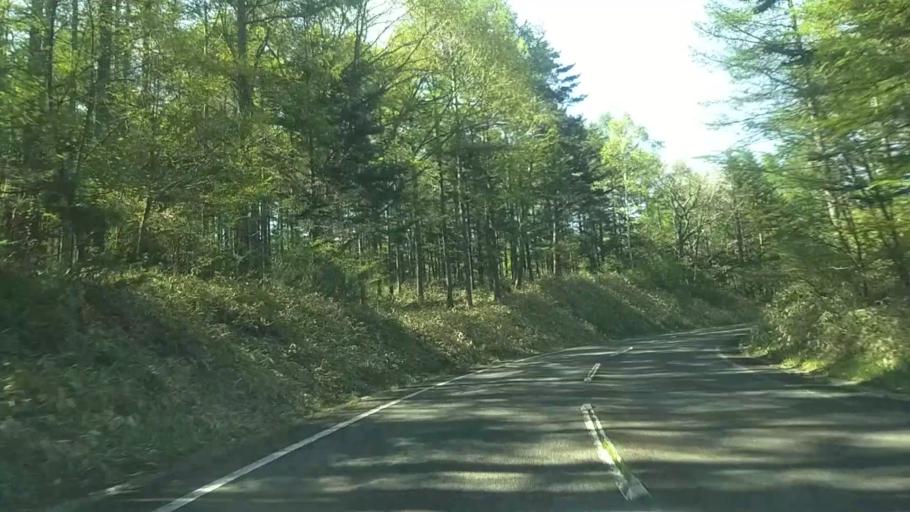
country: JP
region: Yamanashi
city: Nirasaki
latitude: 35.9226
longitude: 138.4014
